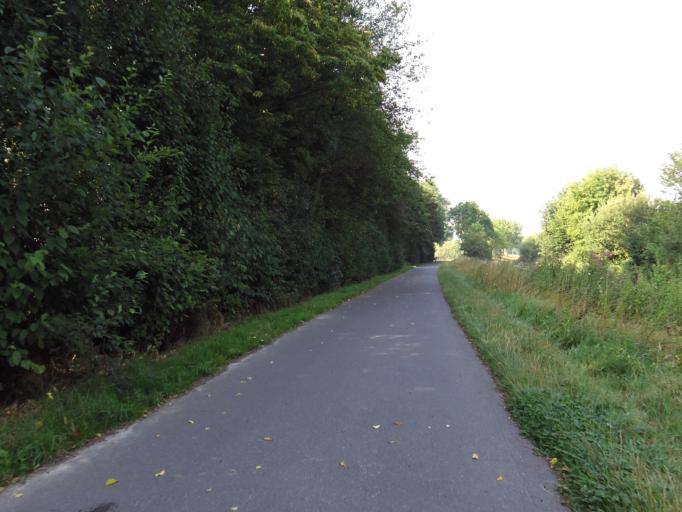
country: DE
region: North Rhine-Westphalia
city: Geilenkirchen
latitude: 50.9759
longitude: 6.1414
